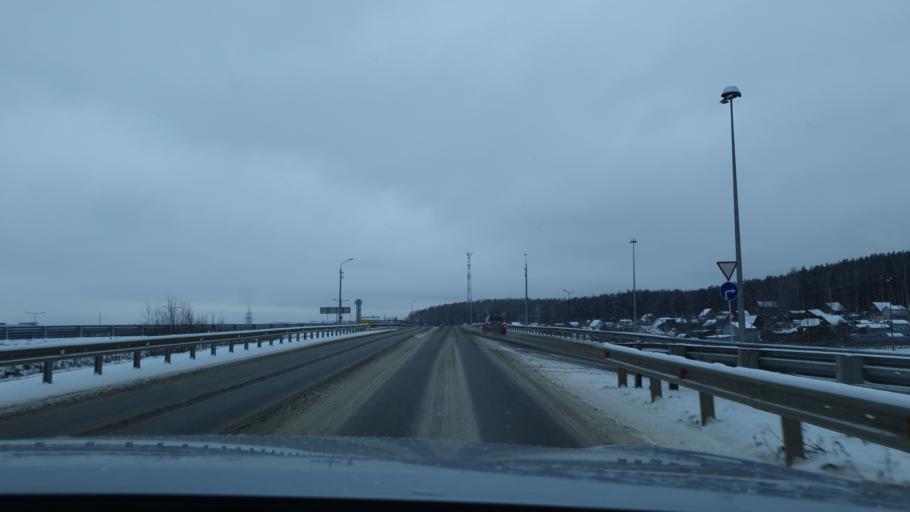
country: RU
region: Sverdlovsk
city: Istok
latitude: 56.7696
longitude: 60.7370
